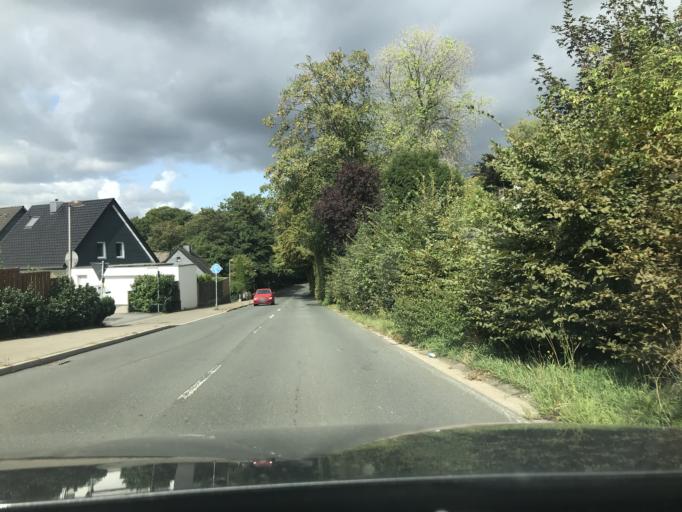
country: DE
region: North Rhine-Westphalia
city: Haan
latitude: 51.1979
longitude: 7.0066
